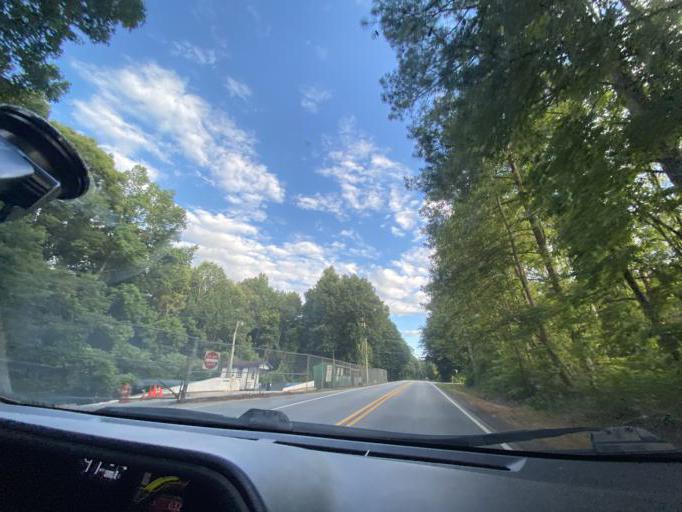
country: US
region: Georgia
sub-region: Fayette County
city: Peachtree City
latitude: 33.4156
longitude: -84.6529
